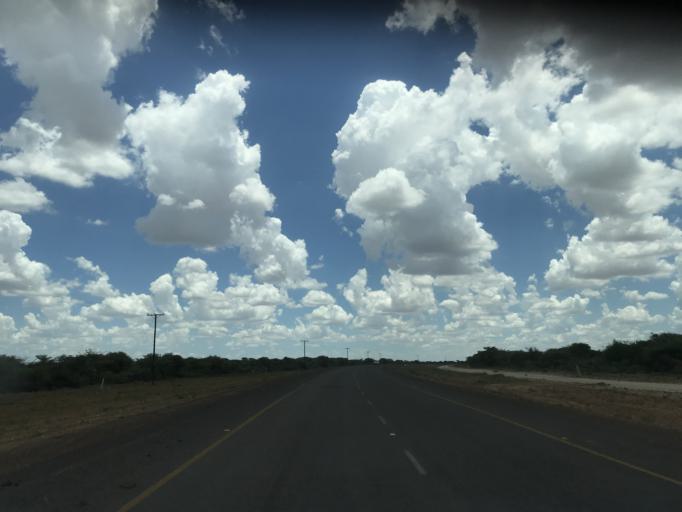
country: BW
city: Mabuli
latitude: -25.8074
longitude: 24.7522
